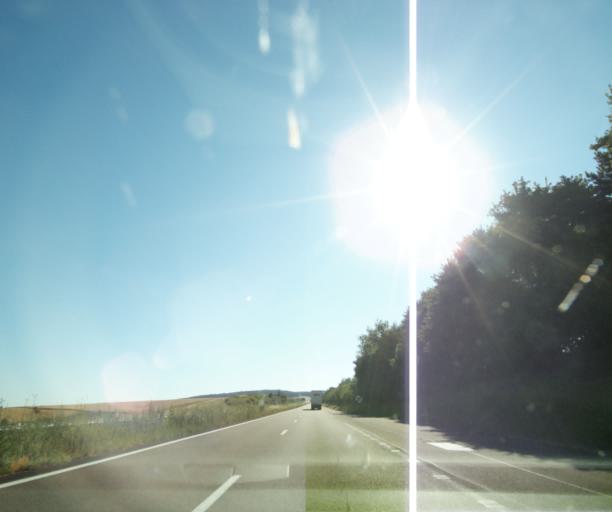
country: FR
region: Champagne-Ardenne
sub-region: Departement de l'Aube
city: Bar-sur-Seine
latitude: 48.1706
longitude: 4.3496
